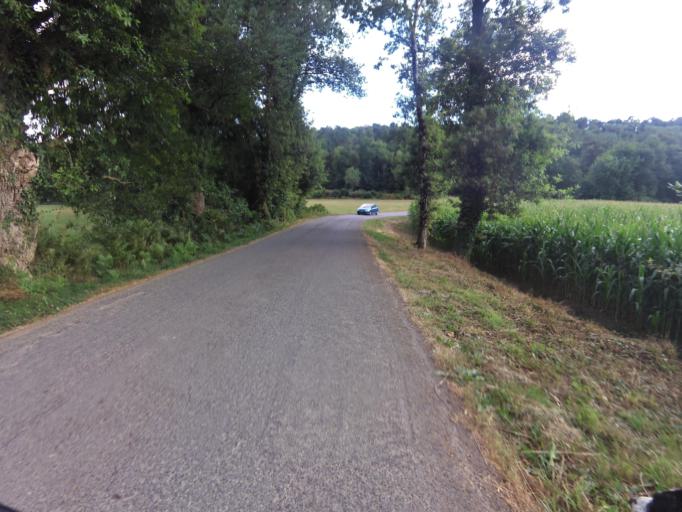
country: FR
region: Brittany
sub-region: Departement du Morbihan
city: Pluherlin
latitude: 47.7101
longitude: -2.3770
